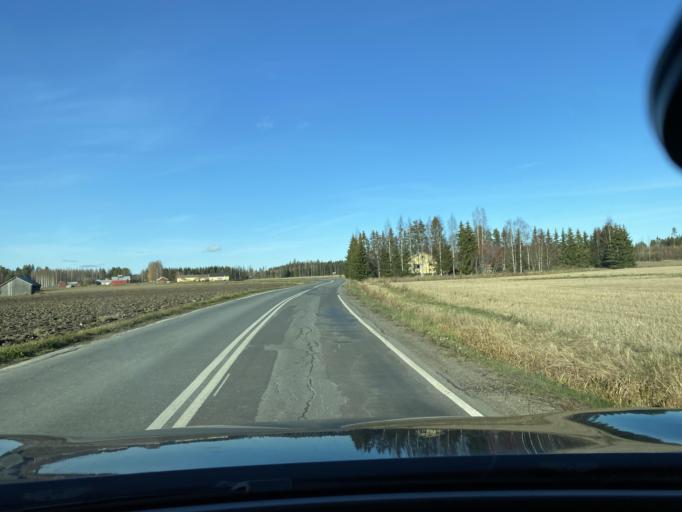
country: FI
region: Haeme
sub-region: Forssa
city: Tammela
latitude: 60.8323
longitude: 23.8402
